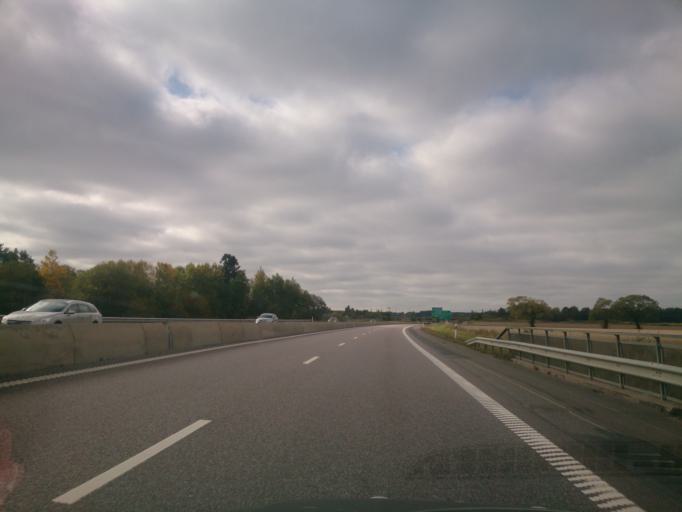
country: SE
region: OEstergoetland
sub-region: Norrkopings Kommun
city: Norrkoping
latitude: 58.5845
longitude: 16.1229
